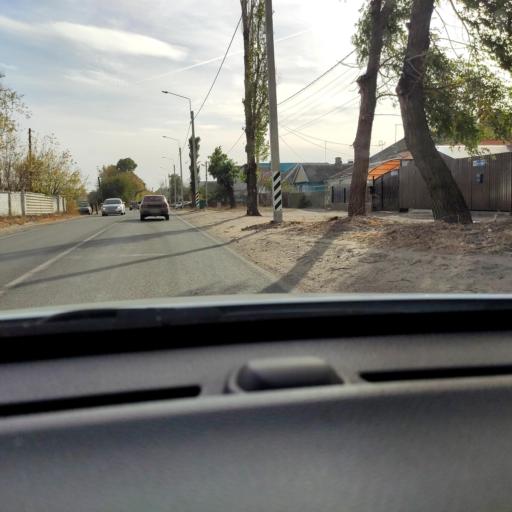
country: RU
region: Voronezj
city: Maslovka
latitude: 51.5653
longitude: 39.2456
